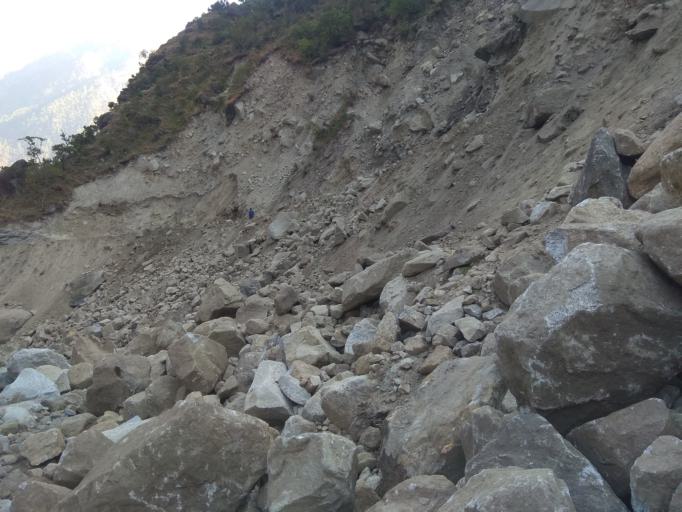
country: NP
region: Far Western
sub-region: Seti Zone
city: Achham
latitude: 29.2289
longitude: 81.6202
